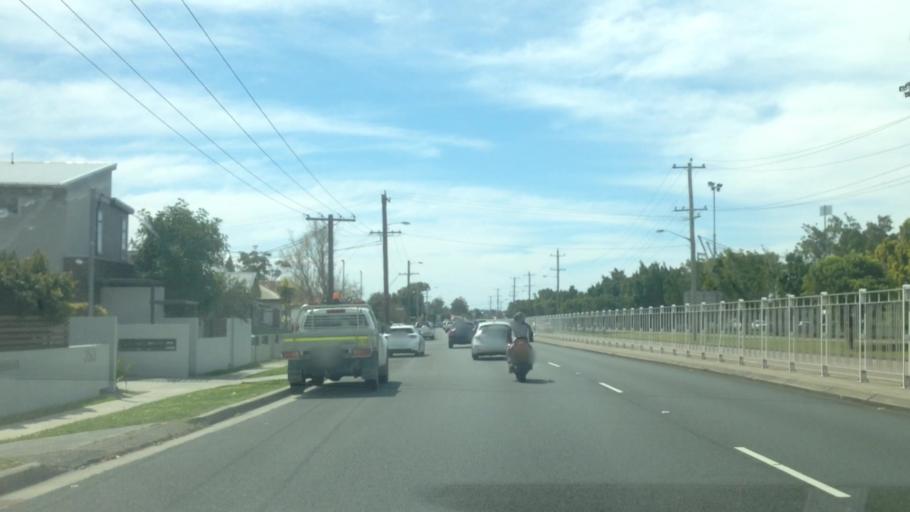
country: AU
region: New South Wales
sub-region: Newcastle
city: Broadmeadow
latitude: -32.9223
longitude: 151.7232
